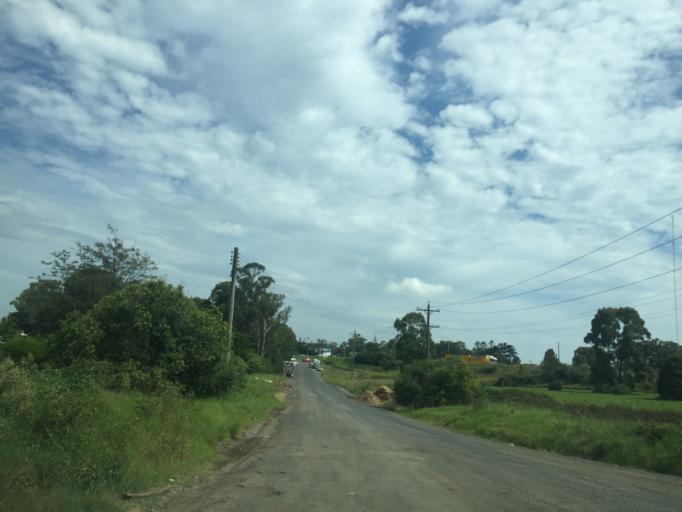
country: AU
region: New South Wales
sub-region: Holroyd
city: Girraween
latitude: -33.8066
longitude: 150.9190
